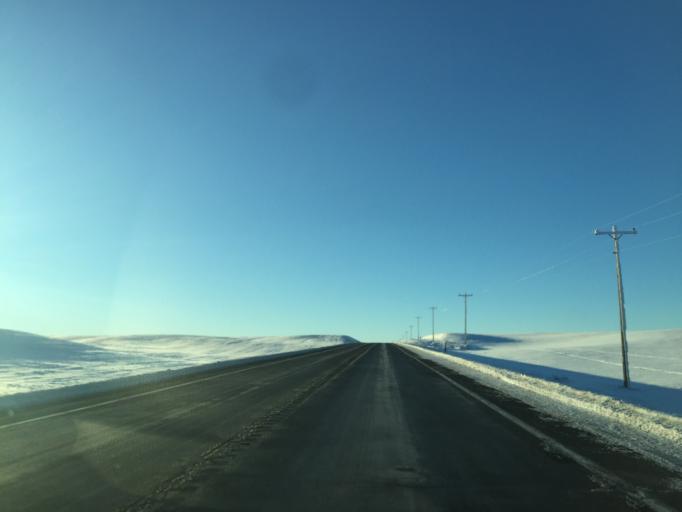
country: US
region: Washington
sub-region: Grant County
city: Soap Lake
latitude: 47.5997
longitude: -119.5218
